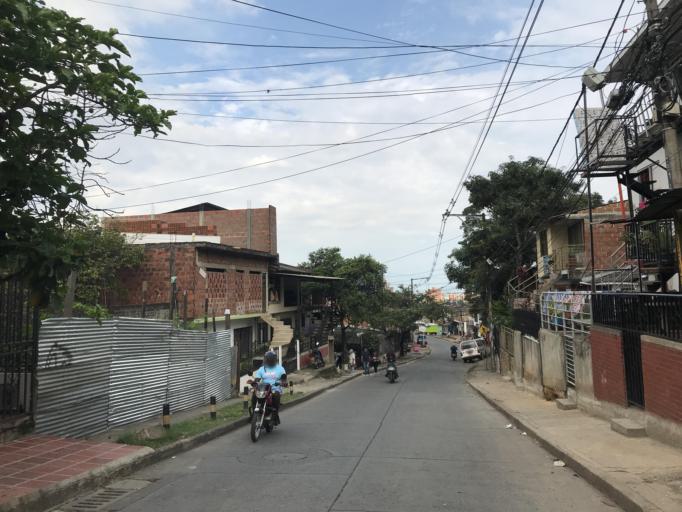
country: CO
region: Valle del Cauca
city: Cali
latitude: 3.3744
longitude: -76.5541
